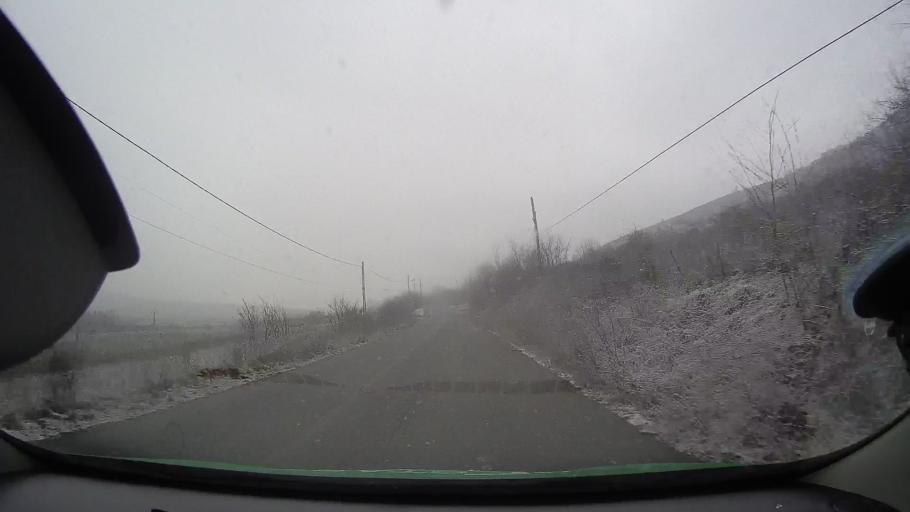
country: RO
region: Alba
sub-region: Comuna Noslac
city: Noslac
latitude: 46.3532
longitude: 23.9330
